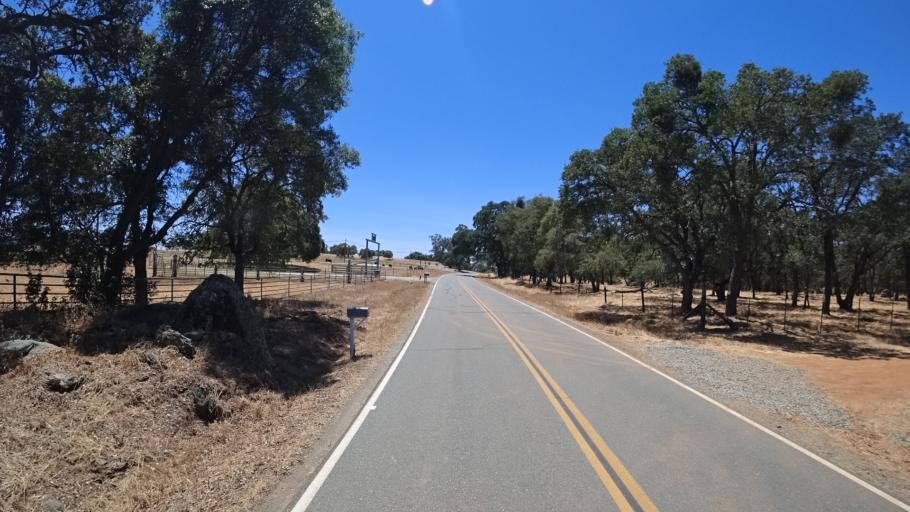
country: US
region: California
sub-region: Calaveras County
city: Valley Springs
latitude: 38.2536
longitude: -120.7721
